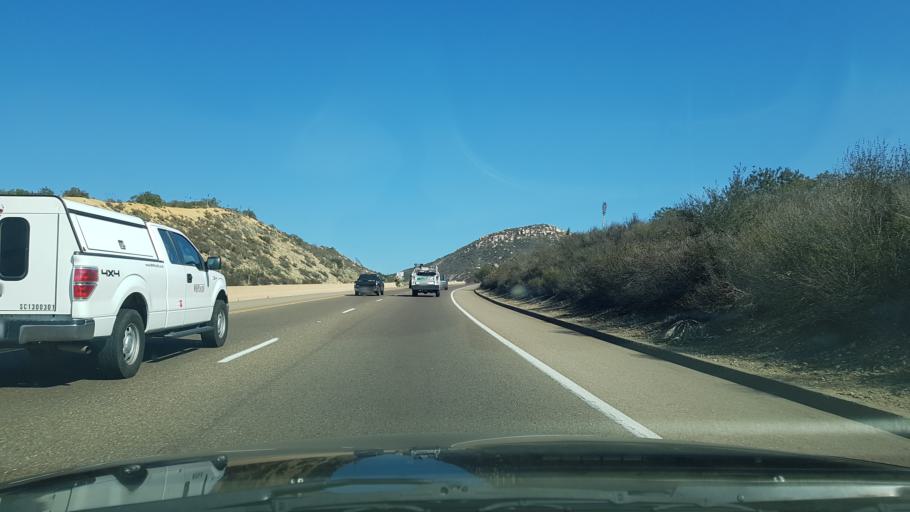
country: US
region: California
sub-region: San Diego County
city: Poway
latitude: 32.9511
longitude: -116.9839
